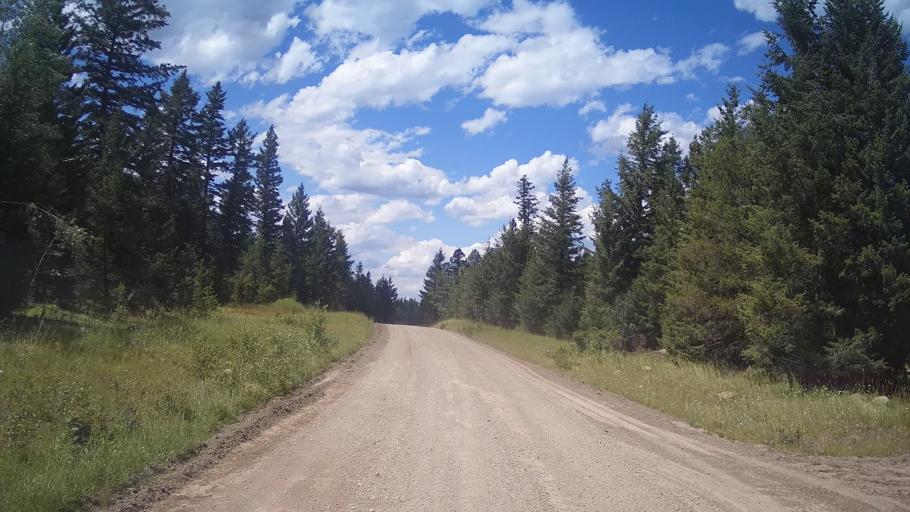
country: CA
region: British Columbia
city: Lillooet
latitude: 51.3211
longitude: -121.8644
